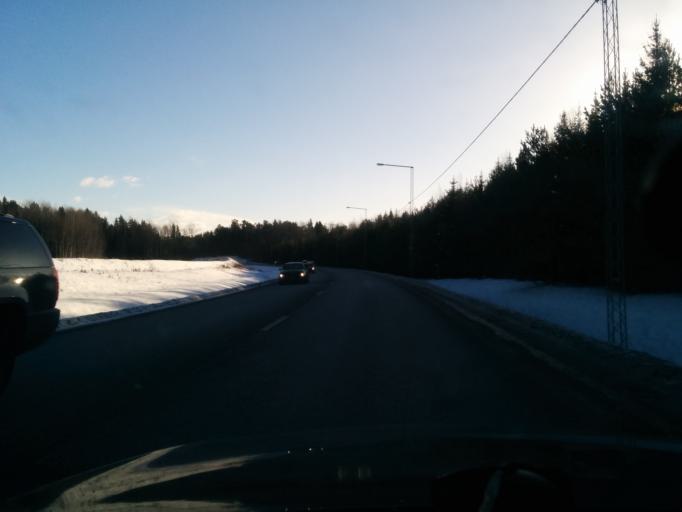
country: SE
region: Stockholm
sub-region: Taby Kommun
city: Taby
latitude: 59.4690
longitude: 18.1154
